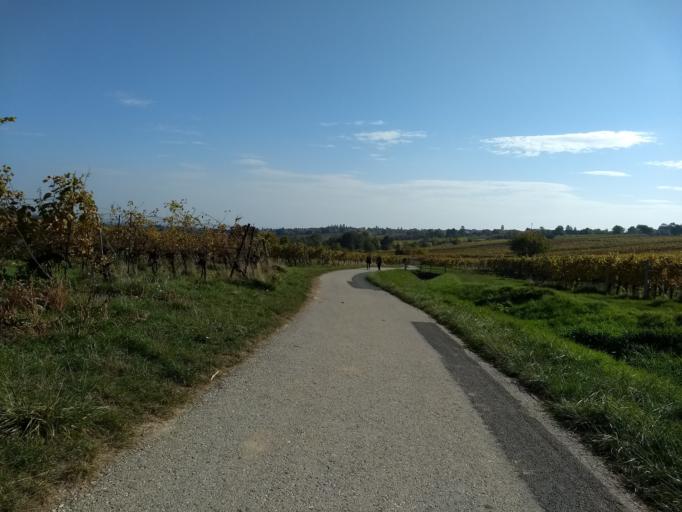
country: AT
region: Lower Austria
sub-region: Politischer Bezirk Modling
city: Giesshubl
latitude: 48.1106
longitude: 16.2410
